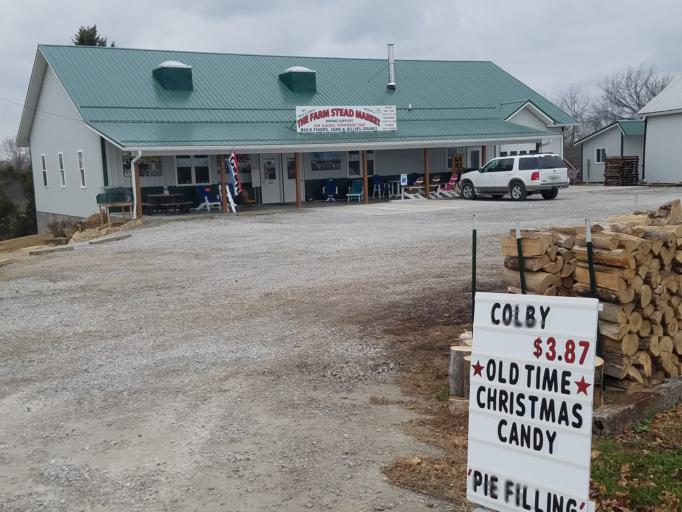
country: US
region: Kentucky
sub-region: Henry County
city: Eminence
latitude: 38.3509
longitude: -85.0337
